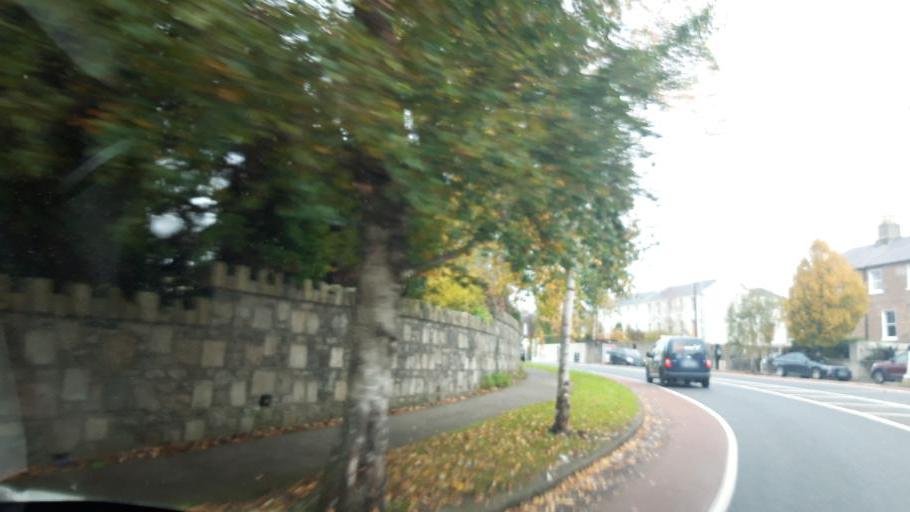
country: IE
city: Clonskeagh
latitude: 53.3160
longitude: -6.2378
